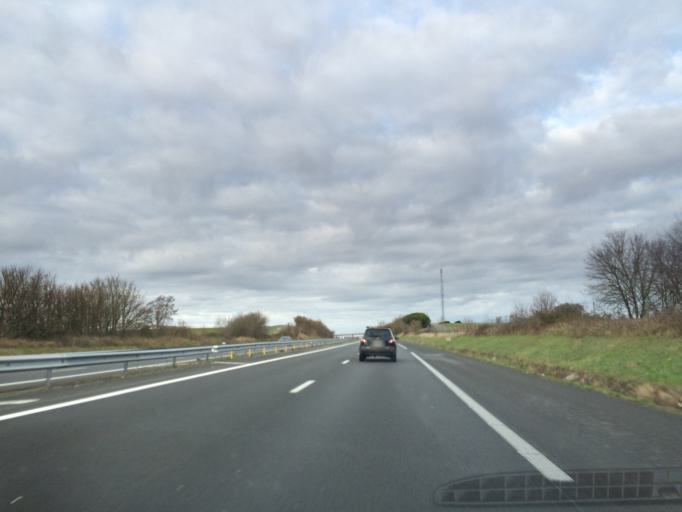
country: FR
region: Poitou-Charentes
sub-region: Departement de la Charente-Maritime
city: Saint-Jean-d'Angely
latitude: 46.0366
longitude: -0.5369
